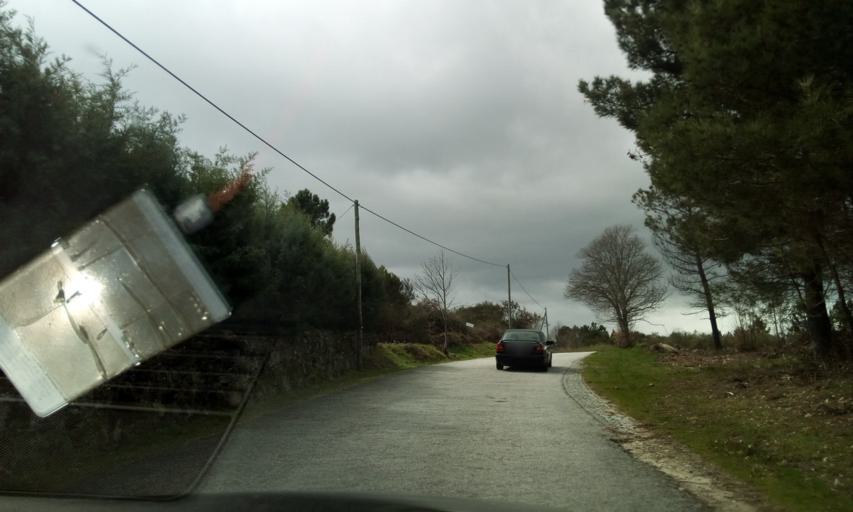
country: PT
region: Guarda
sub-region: Fornos de Algodres
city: Fornos de Algodres
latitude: 40.6369
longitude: -7.5654
